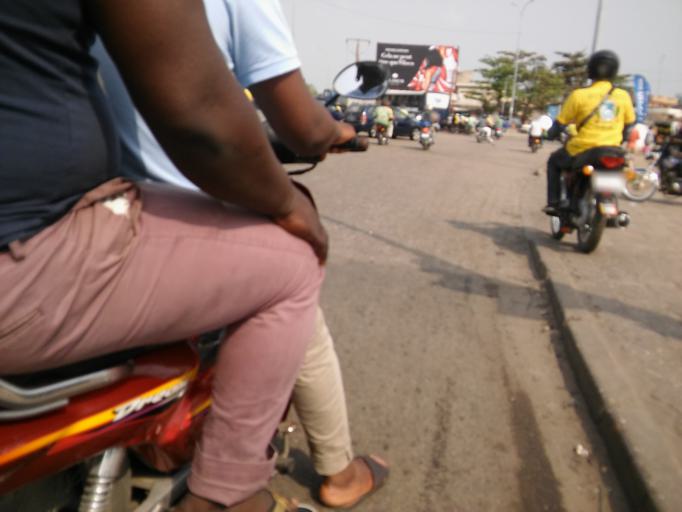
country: BJ
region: Littoral
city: Cotonou
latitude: 6.3770
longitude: 2.3893
